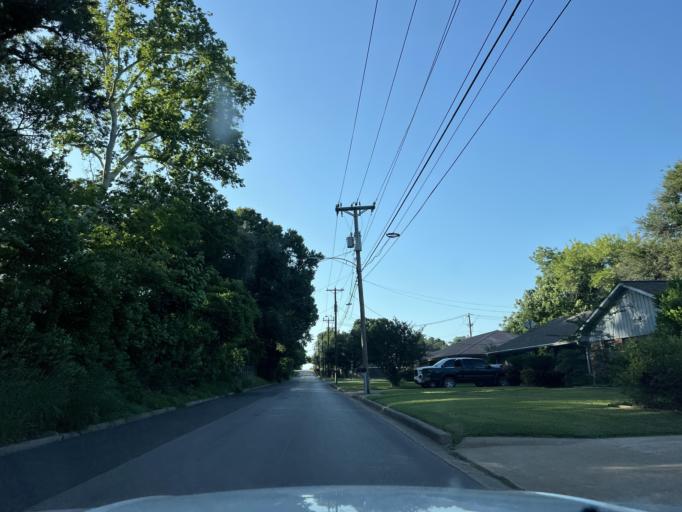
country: US
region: Texas
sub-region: Washington County
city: Brenham
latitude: 30.1544
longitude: -96.3858
